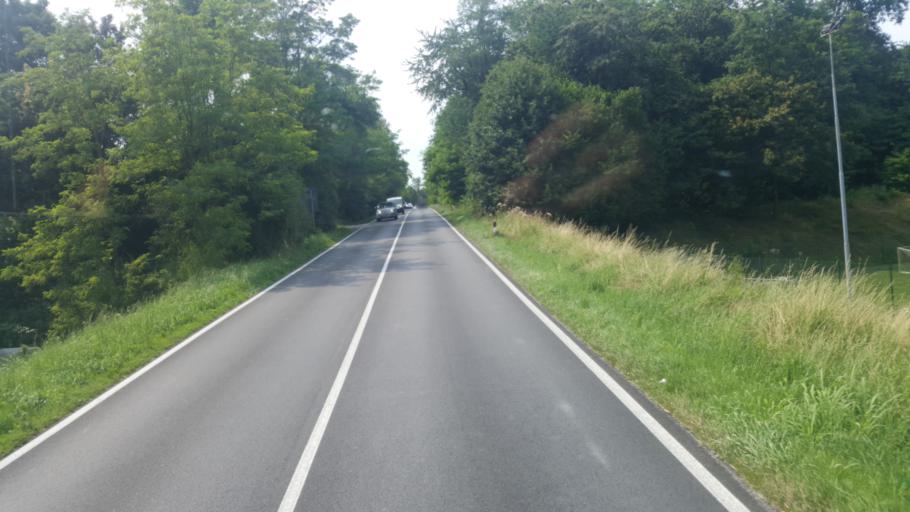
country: IT
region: Lombardy
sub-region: Provincia di Como
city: Oltrona di San Mamette
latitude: 45.7484
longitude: 8.9788
